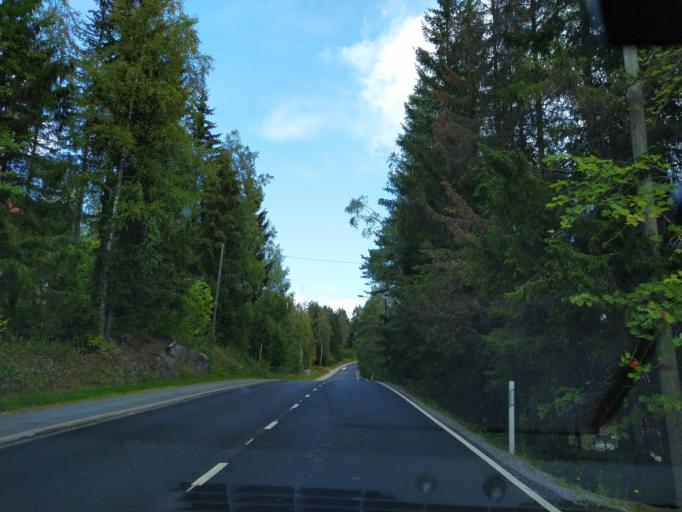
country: FI
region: Pirkanmaa
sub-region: Tampere
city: Kuru
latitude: 61.8884
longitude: 23.7393
